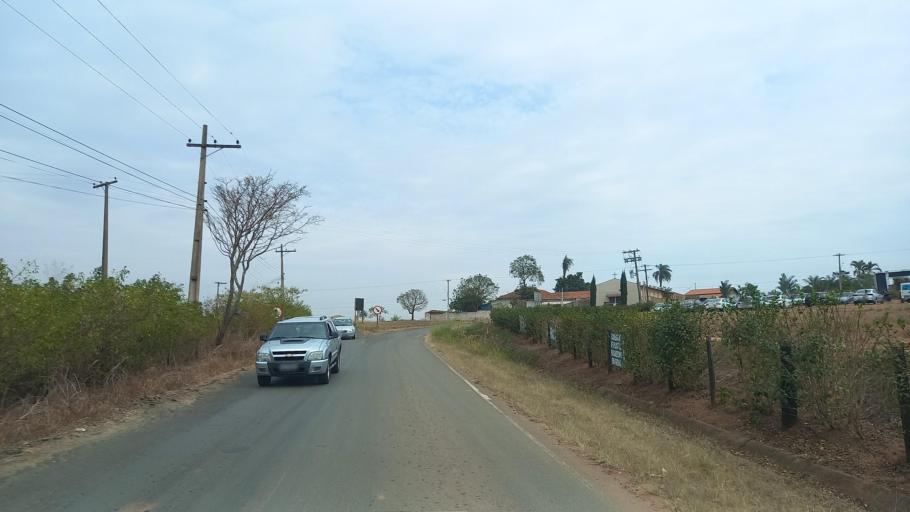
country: BR
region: Sao Paulo
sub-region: Moji-Guacu
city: Mogi-Gaucu
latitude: -22.3319
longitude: -46.8794
